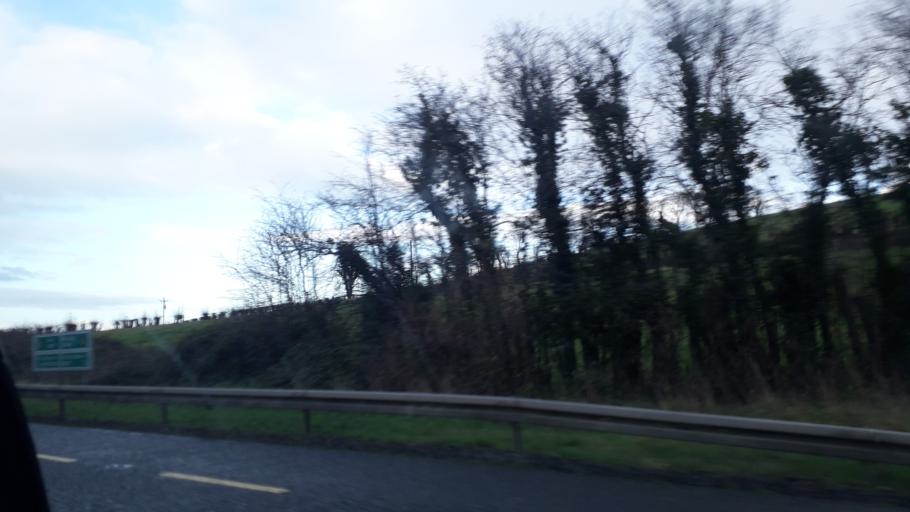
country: IE
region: Ulster
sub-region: County Monaghan
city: Carrickmacross
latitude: 53.9339
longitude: -6.6529
